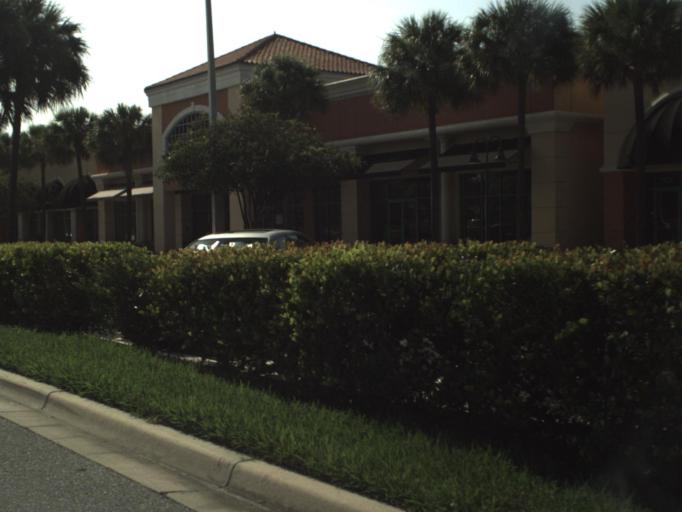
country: US
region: Florida
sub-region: Broward County
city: Margate
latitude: 26.2722
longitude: -80.2267
